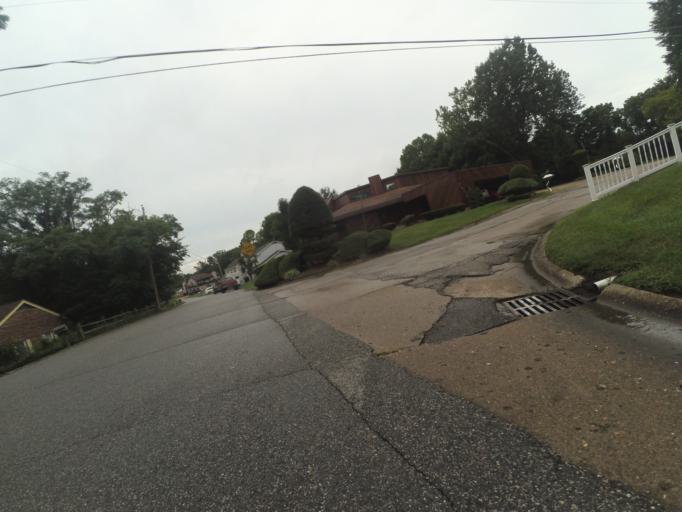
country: US
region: West Virginia
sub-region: Cabell County
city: Huntington
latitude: 38.4003
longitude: -82.4521
